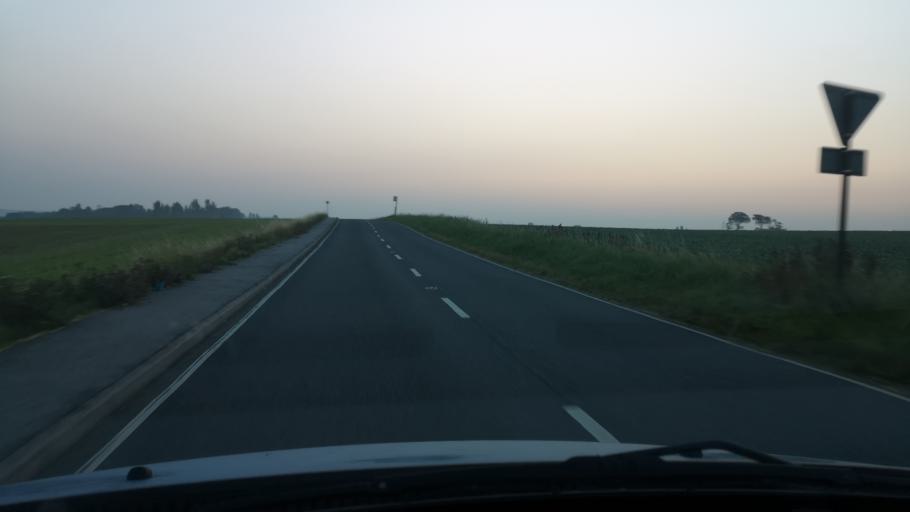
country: GB
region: England
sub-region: City and Borough of Wakefield
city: Badsworth
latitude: 53.6257
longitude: -1.3134
